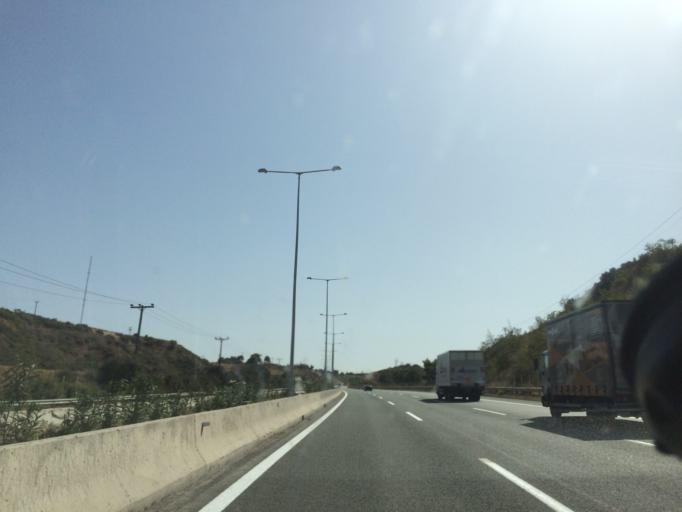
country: GR
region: Attica
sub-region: Nomarchia Anatolikis Attikis
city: Agios Stefanos
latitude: 38.1599
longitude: 23.8555
